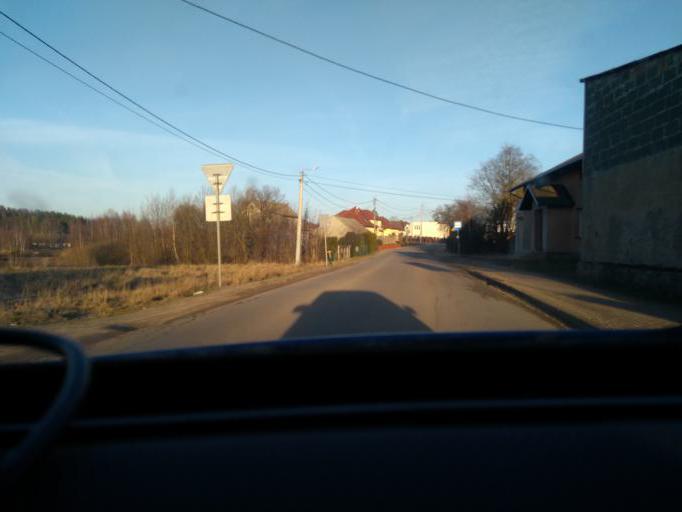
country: PL
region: Pomeranian Voivodeship
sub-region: Powiat kartuski
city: Przodkowo
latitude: 54.4141
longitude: 18.3134
